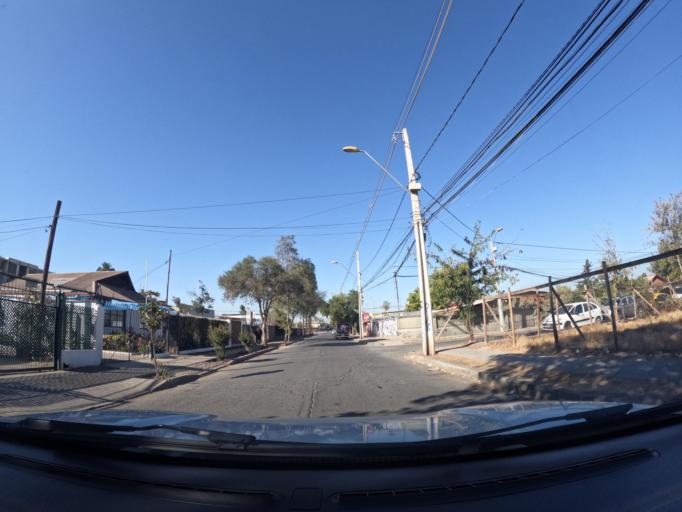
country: CL
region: Santiago Metropolitan
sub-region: Provincia de Santiago
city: Villa Presidente Frei, Nunoa, Santiago, Chile
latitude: -33.5095
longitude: -70.5786
